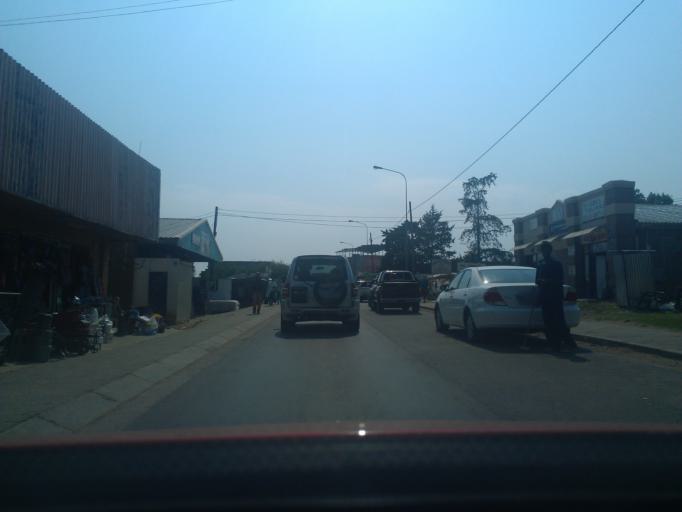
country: LS
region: Berea
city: Teyateyaneng
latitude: -29.1496
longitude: 27.7464
